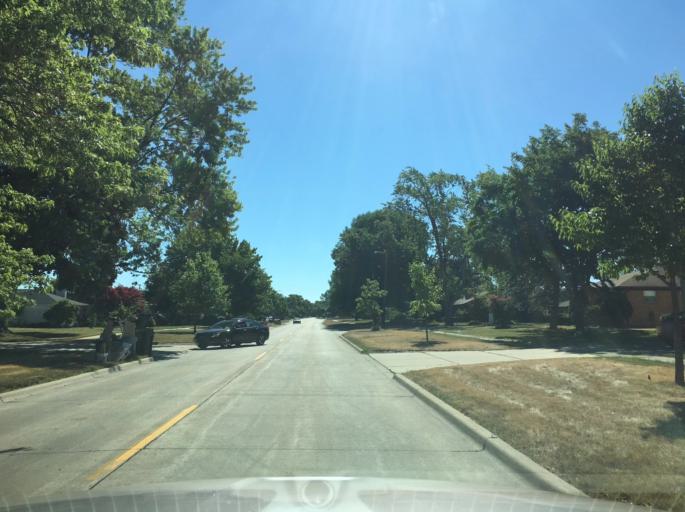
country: US
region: Michigan
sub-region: Macomb County
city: Saint Clair Shores
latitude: 42.5029
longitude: -82.9014
